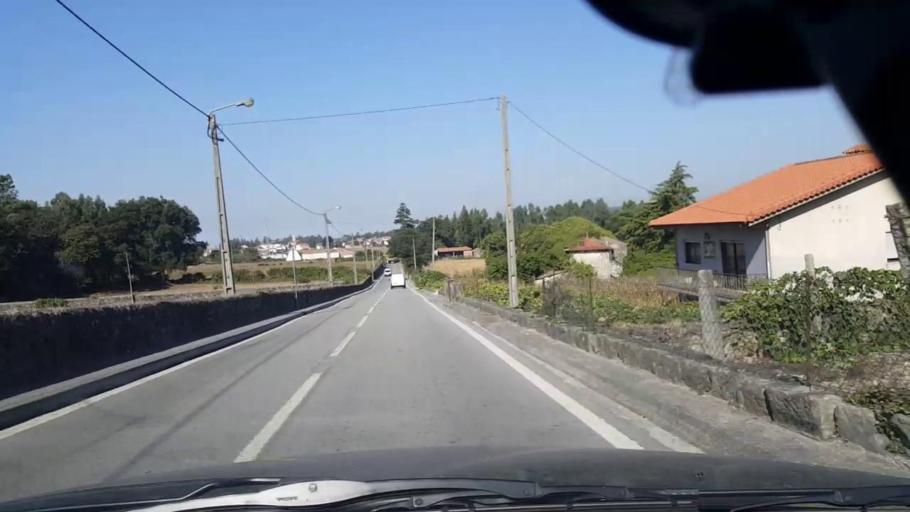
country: PT
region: Porto
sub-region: Vila do Conde
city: Arvore
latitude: 41.3752
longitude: -8.6709
